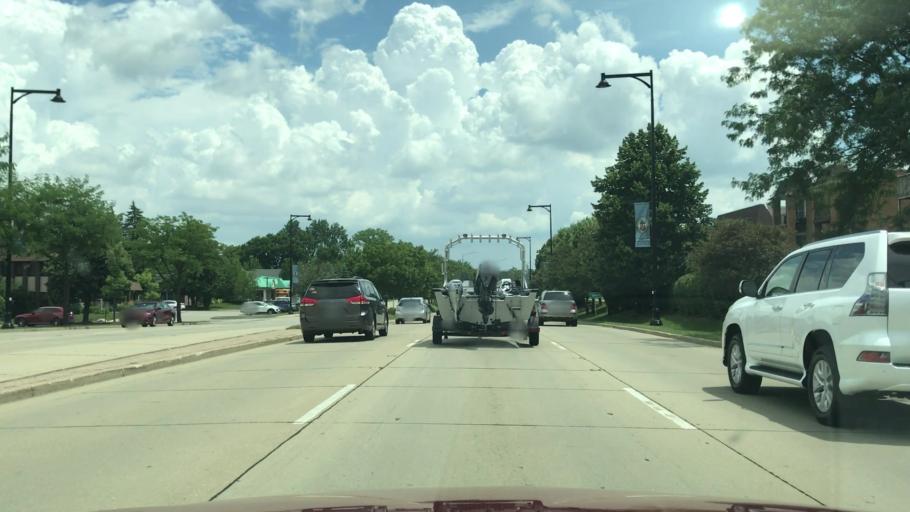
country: US
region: Illinois
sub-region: DuPage County
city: Bloomingdale
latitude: 41.9569
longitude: -88.0646
